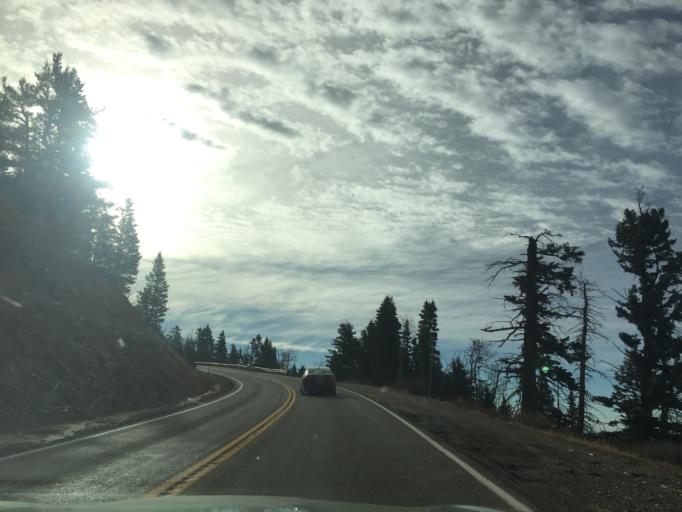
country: US
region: Utah
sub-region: Iron County
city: Cedar City
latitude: 37.5804
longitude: -112.8725
